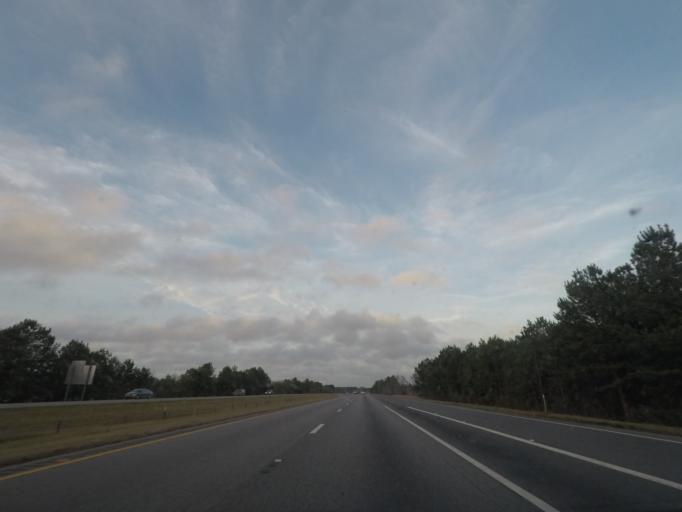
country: US
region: South Carolina
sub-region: Orangeburg County
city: Holly Hill
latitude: 33.3873
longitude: -80.5168
